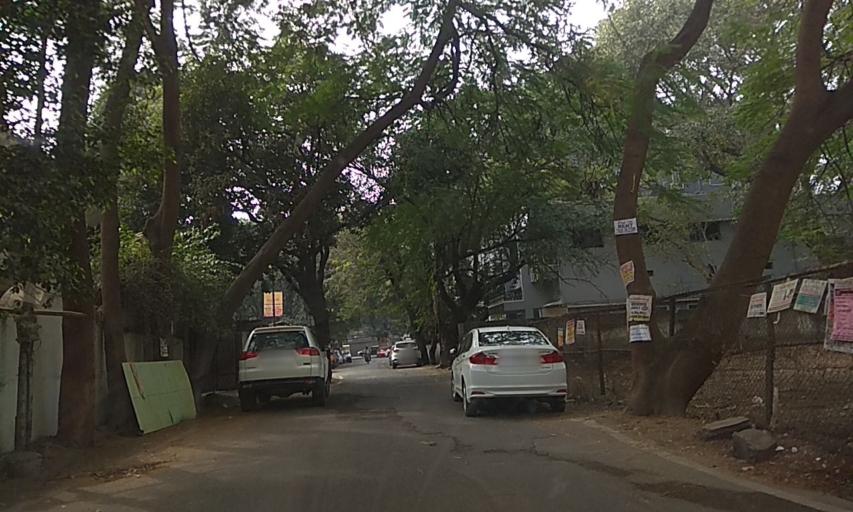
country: IN
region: Maharashtra
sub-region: Pune Division
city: Pune
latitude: 18.5032
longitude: 73.9293
